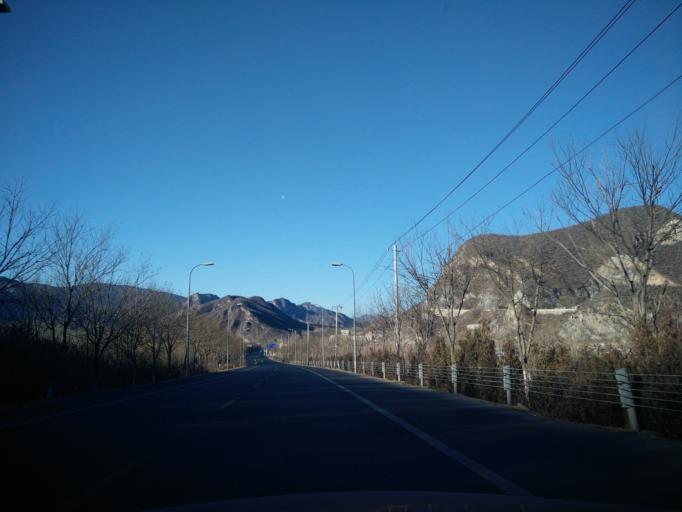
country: CN
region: Beijing
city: Miaofengshan
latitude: 39.9900
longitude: 116.0686
